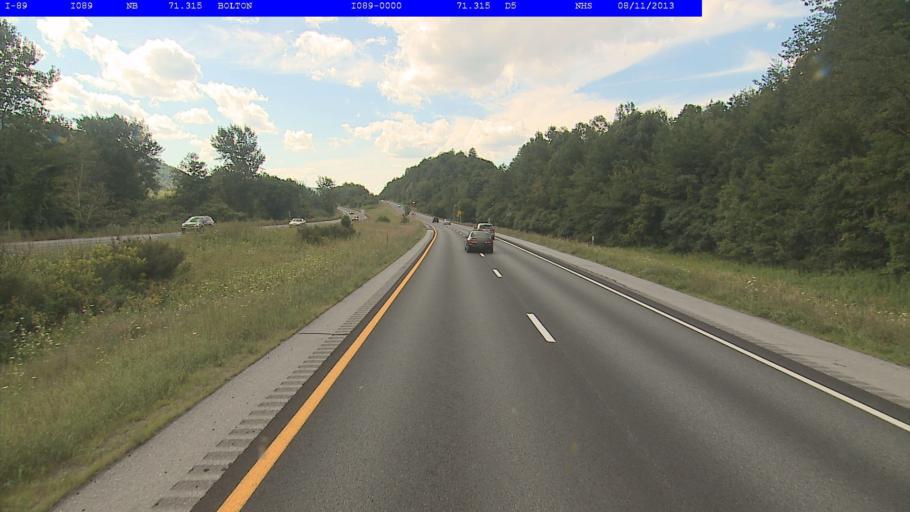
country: US
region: Vermont
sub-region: Washington County
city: Waterbury
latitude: 44.3772
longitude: -72.8927
